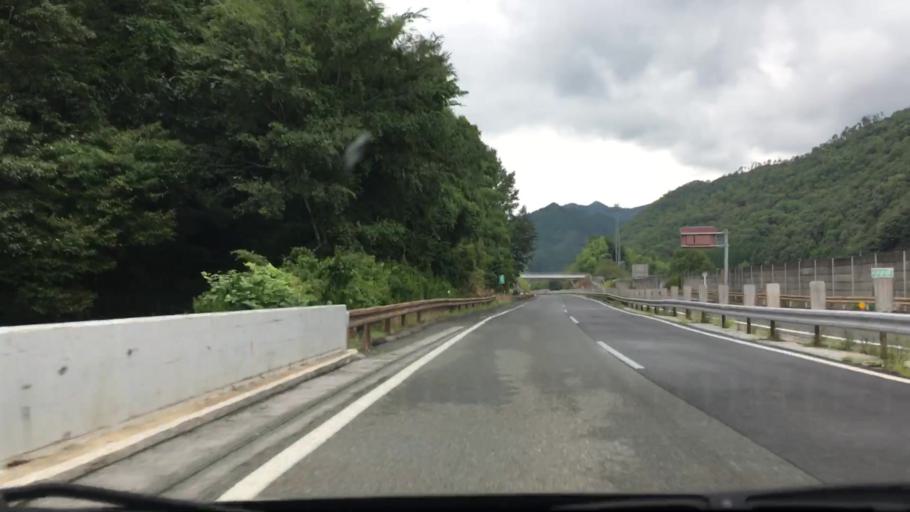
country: JP
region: Okayama
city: Niimi
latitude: 35.0014
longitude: 133.4434
